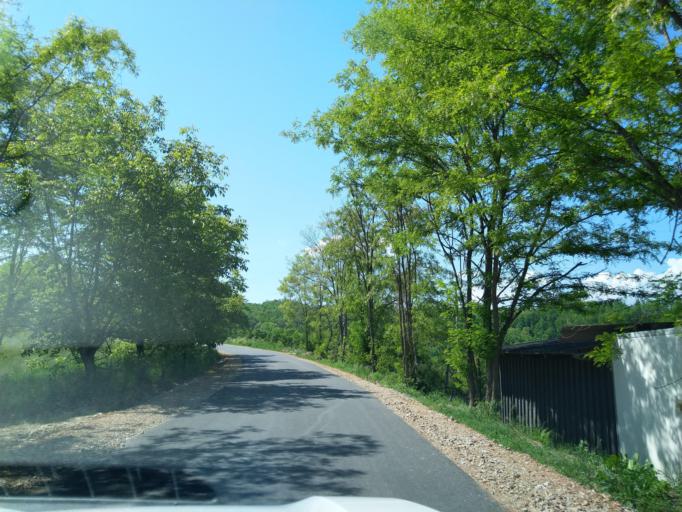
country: RS
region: Central Serbia
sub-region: Zlatiborski Okrug
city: Uzice
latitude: 43.8607
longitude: 19.9274
